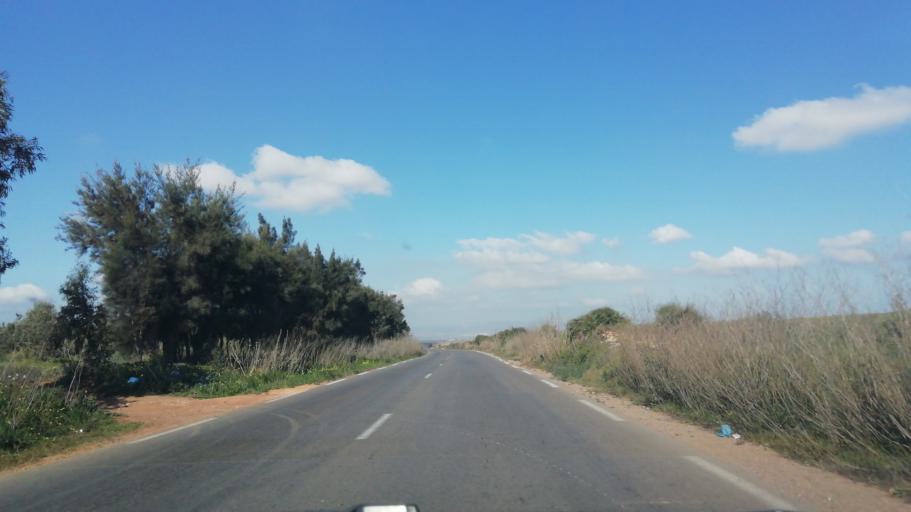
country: DZ
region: Oran
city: Ain el Bya
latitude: 35.7196
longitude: -0.2385
